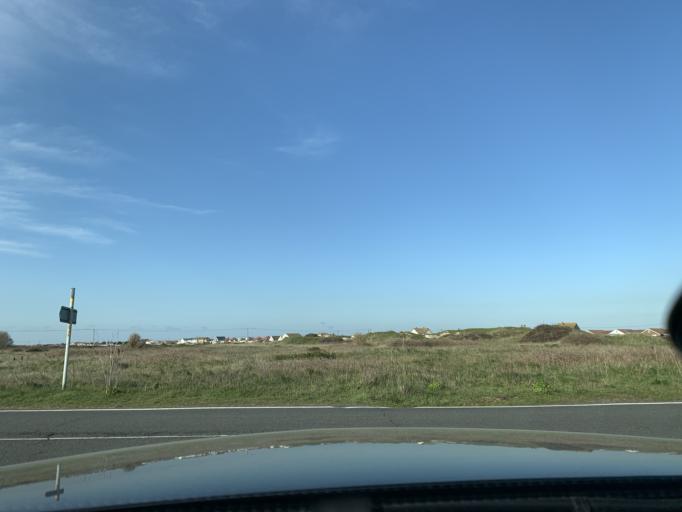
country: GB
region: England
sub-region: Kent
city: New Romney
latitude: 50.9288
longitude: 0.9707
